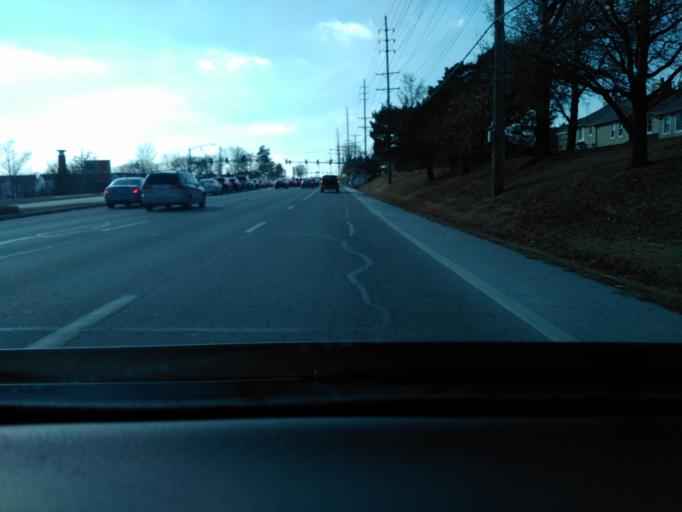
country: US
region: Missouri
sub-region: Saint Louis County
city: Manchester
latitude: 38.6233
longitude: -90.5187
